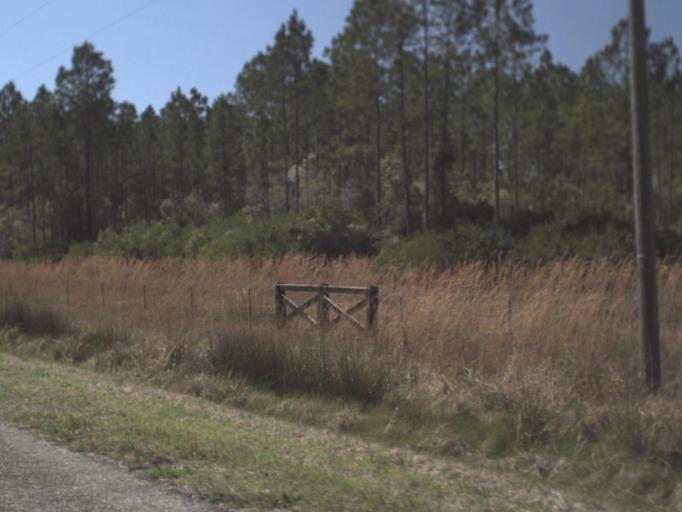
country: US
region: Florida
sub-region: Leon County
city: Woodville
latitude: 30.2078
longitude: -84.0498
